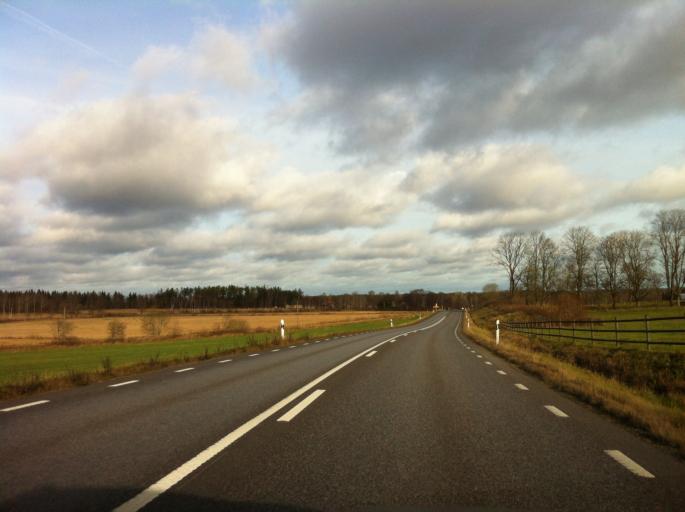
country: SE
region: Kronoberg
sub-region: Vaxjo Kommun
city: Gemla
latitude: 56.7875
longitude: 14.6151
